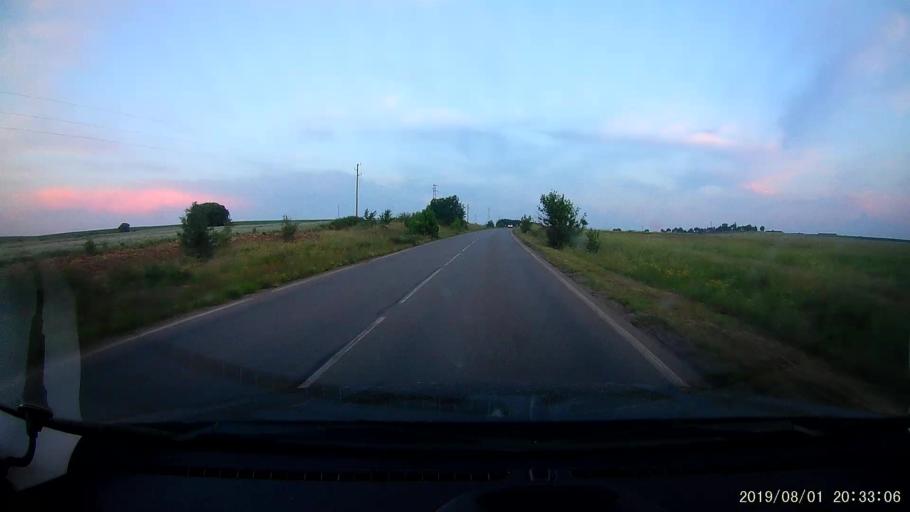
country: BG
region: Yambol
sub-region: Obshtina Elkhovo
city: Elkhovo
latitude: 42.1113
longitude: 26.5317
